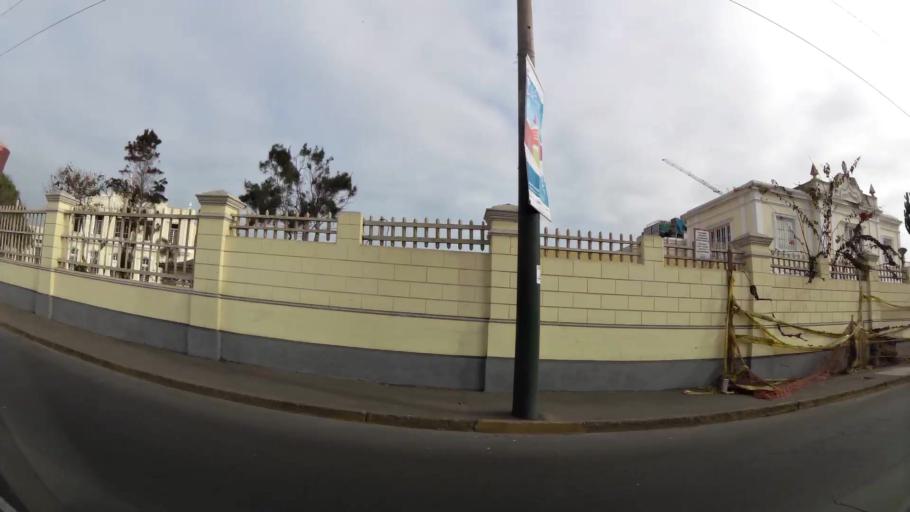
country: PE
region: Lima
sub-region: Lima
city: San Isidro
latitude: -12.0987
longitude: -77.0680
